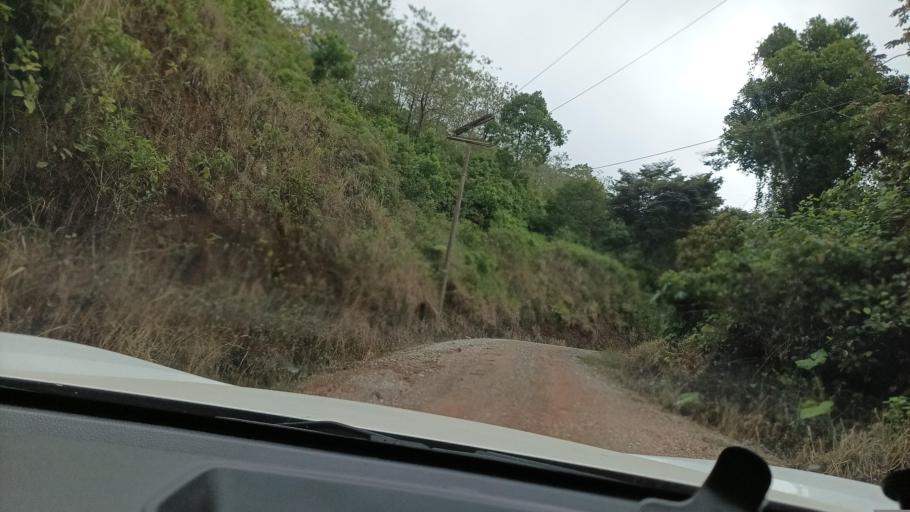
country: MX
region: Veracruz
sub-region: Uxpanapa
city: Poblado 10
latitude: 17.4211
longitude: -94.4161
